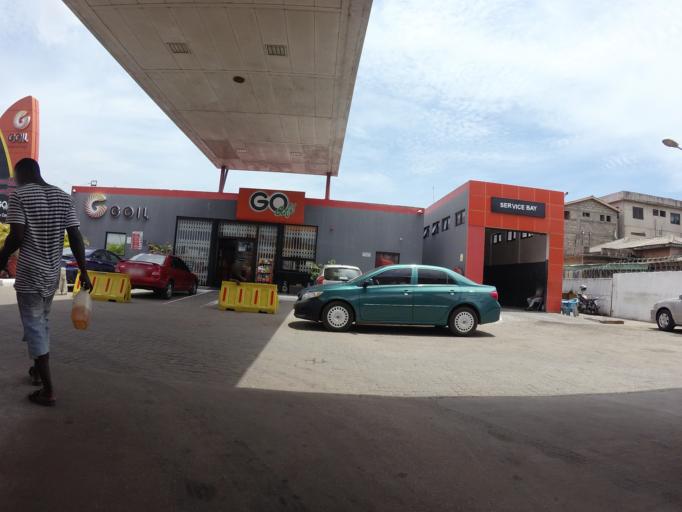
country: GH
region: Greater Accra
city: Accra
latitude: 5.5629
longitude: -0.2326
